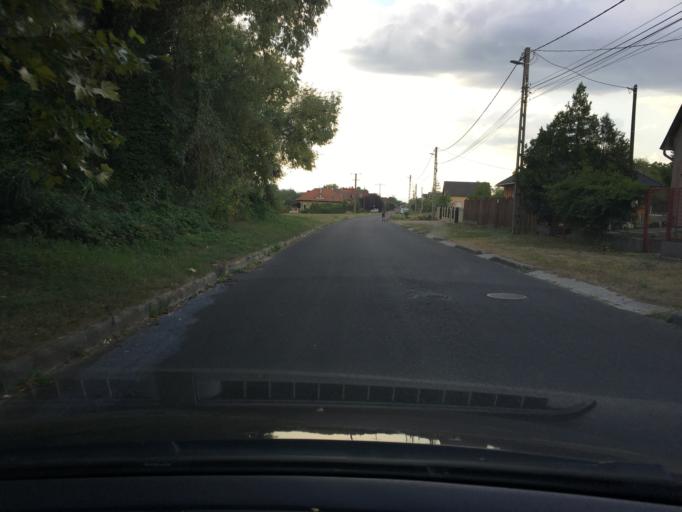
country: HU
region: Pest
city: Veresegyhaz
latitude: 47.6462
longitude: 19.3022
